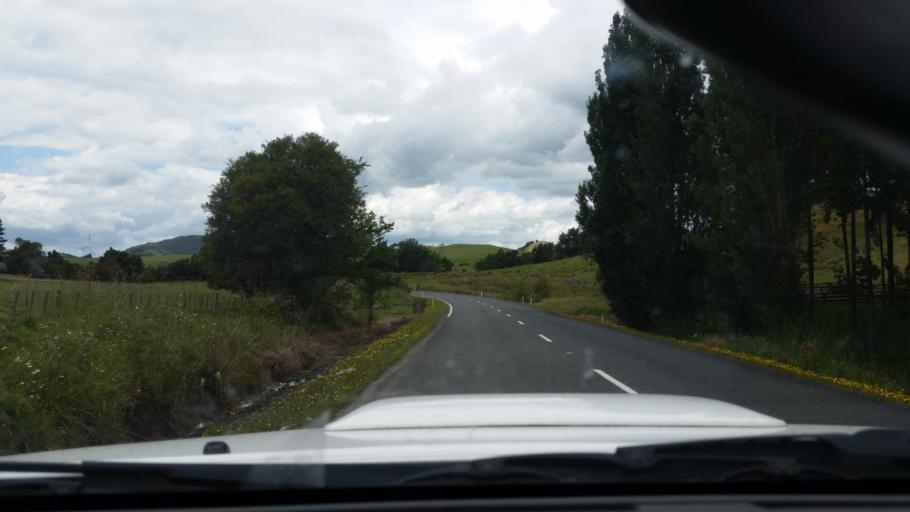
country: NZ
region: Northland
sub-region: Kaipara District
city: Dargaville
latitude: -35.7486
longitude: 173.8784
